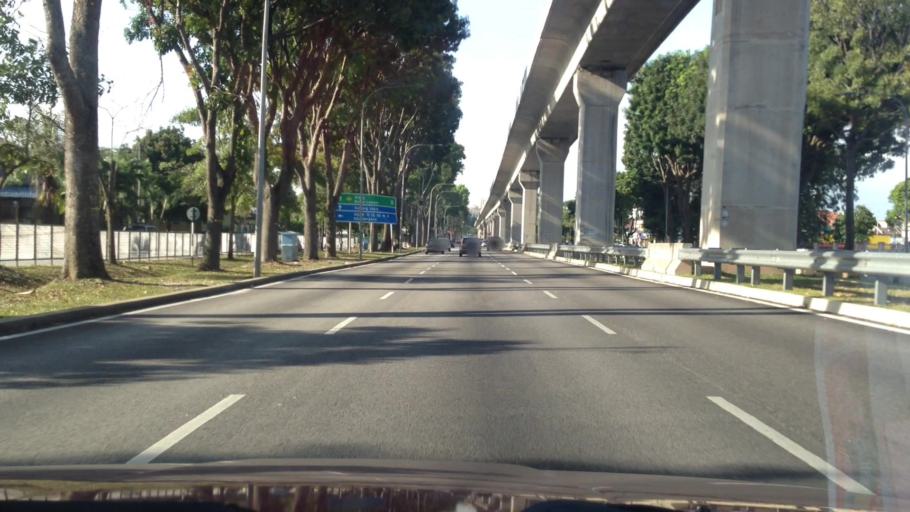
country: MY
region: Selangor
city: Subang Jaya
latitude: 3.0364
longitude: 101.5881
